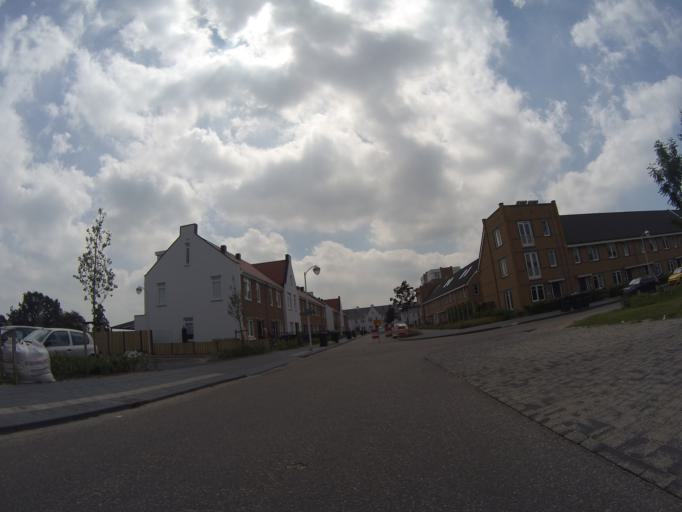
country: NL
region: Utrecht
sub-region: Gemeente Amersfoort
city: Randenbroek
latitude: 52.1918
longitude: 5.4252
